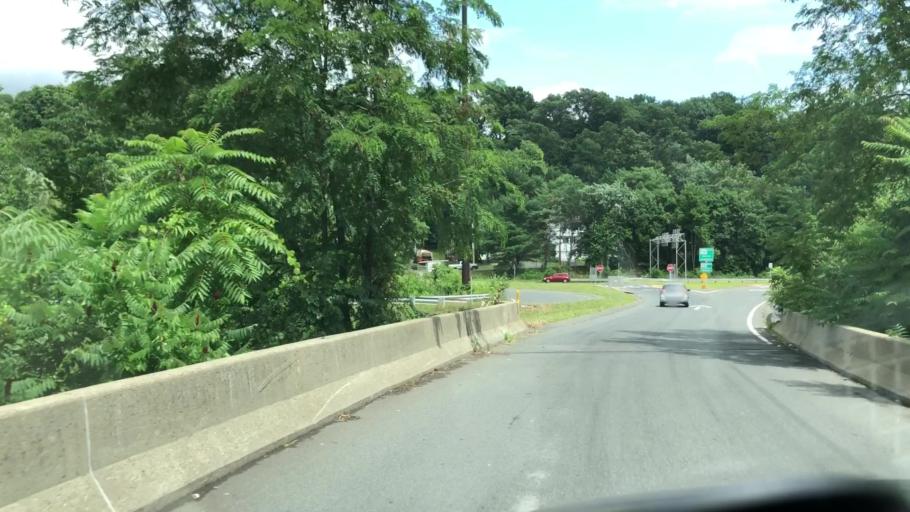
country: US
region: Massachusetts
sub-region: Hampden County
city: Chicopee
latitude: 42.1519
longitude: -72.6111
